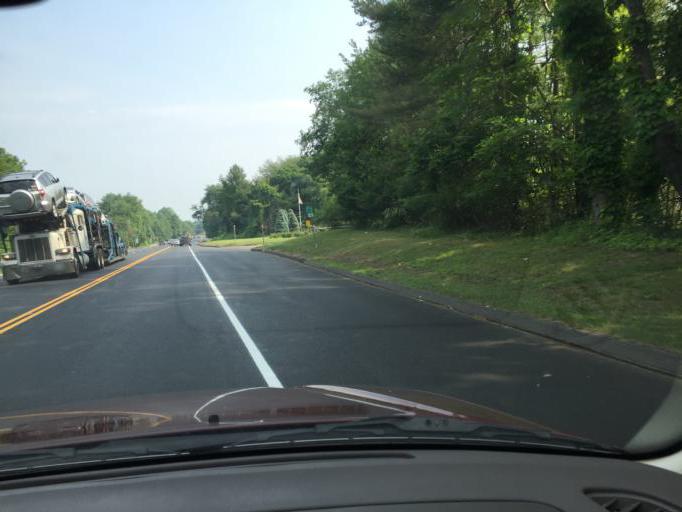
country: US
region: Connecticut
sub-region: Fairfield County
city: Westport
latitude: 41.1308
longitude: -73.3339
